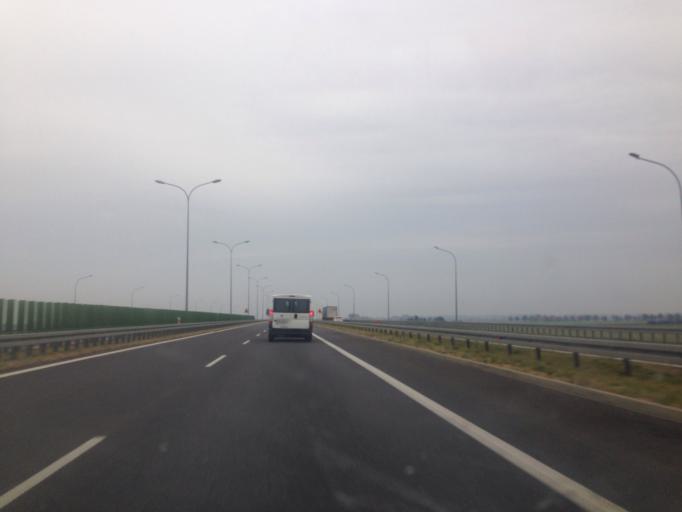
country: PL
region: Greater Poland Voivodeship
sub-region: Powiat poznanski
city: Kostrzyn
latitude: 52.3949
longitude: 17.2555
